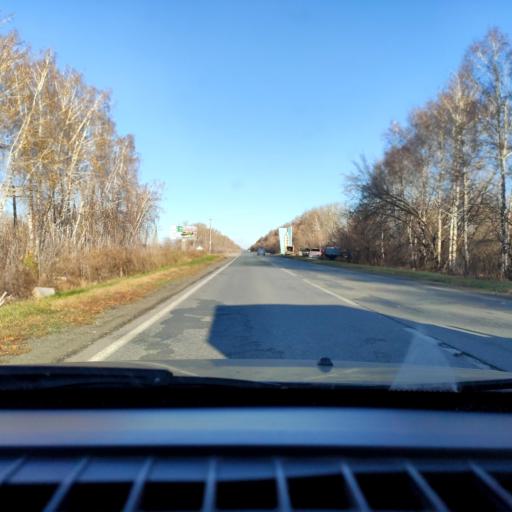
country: RU
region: Samara
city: Tol'yatti
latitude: 53.5959
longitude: 49.3257
